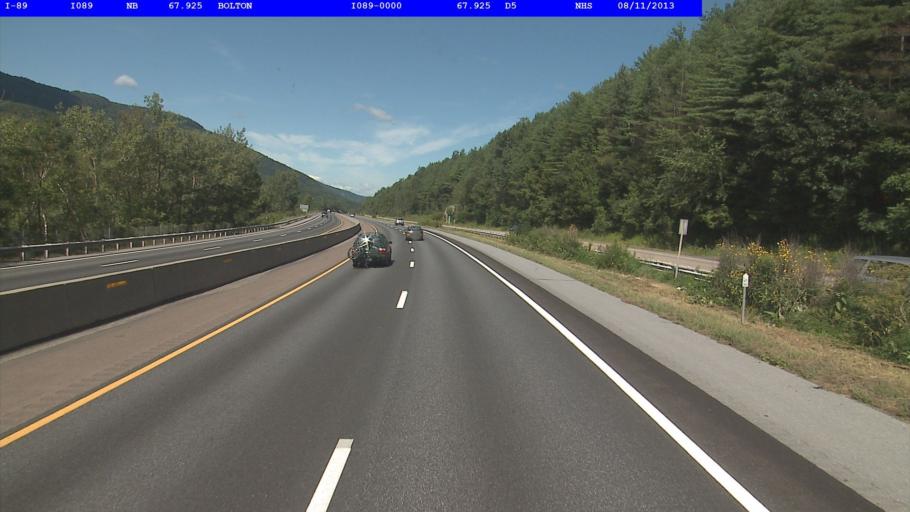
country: US
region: Vermont
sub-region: Washington County
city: Waterbury
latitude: 44.3611
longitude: -72.8283
